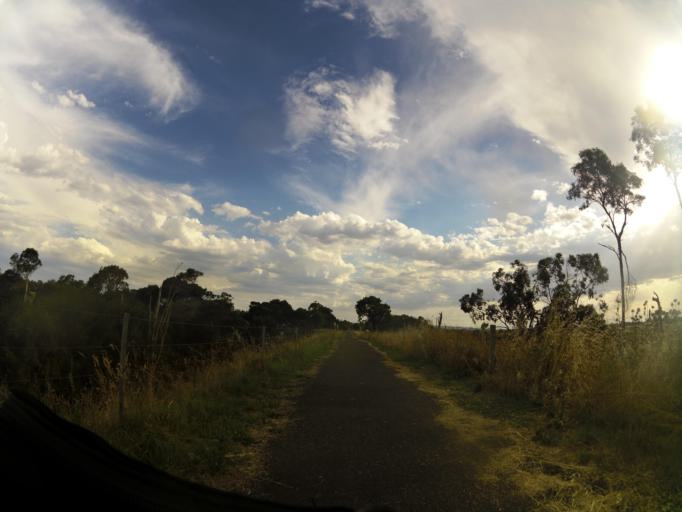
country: AU
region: Victoria
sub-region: Latrobe
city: Traralgon
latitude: -38.1673
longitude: 146.5657
